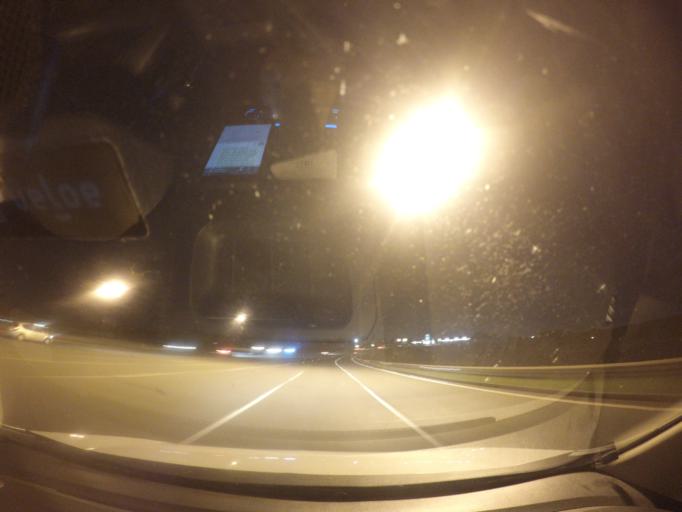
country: BR
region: Sao Paulo
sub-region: Sumare
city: Sumare
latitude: -22.7725
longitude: -47.2374
